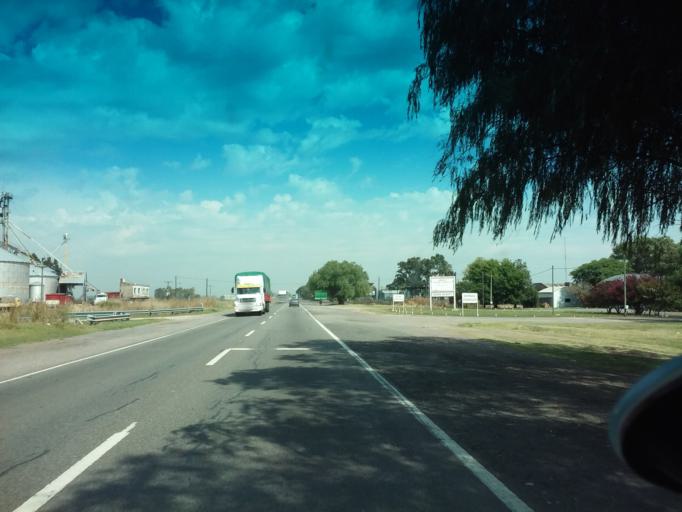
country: AR
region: Buenos Aires
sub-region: Partido de Carlos Casares
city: Carlos Casares
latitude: -35.6327
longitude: -61.3442
